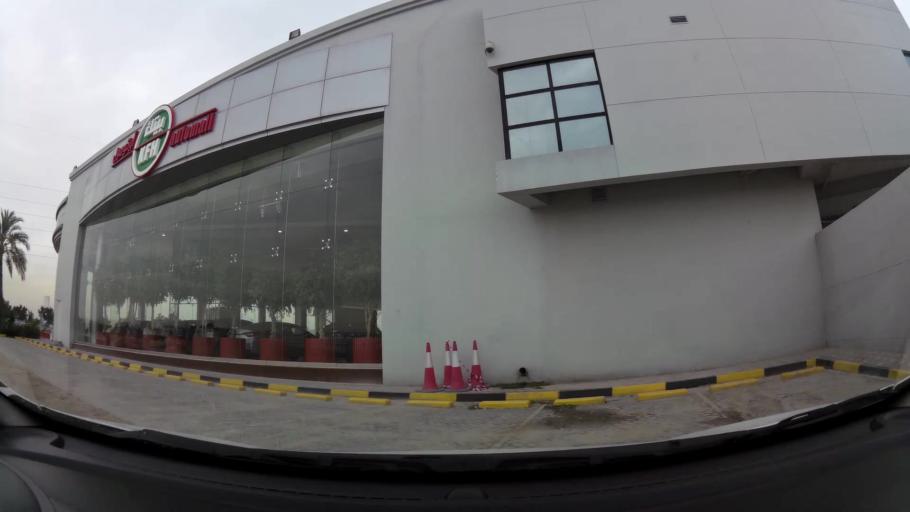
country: BH
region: Northern
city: Sitrah
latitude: 26.1684
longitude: 50.6050
